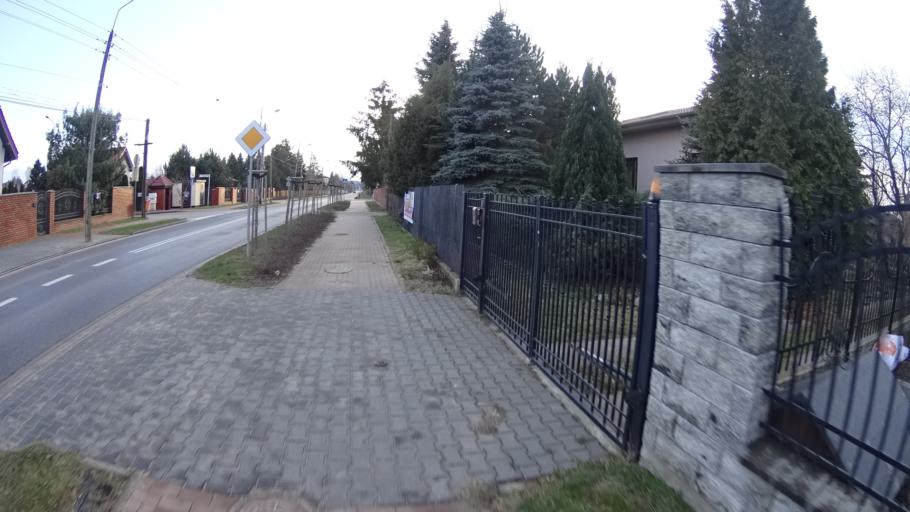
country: PL
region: Masovian Voivodeship
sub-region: Powiat warszawski zachodni
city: Ozarow Mazowiecki
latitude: 52.2209
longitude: 20.8008
